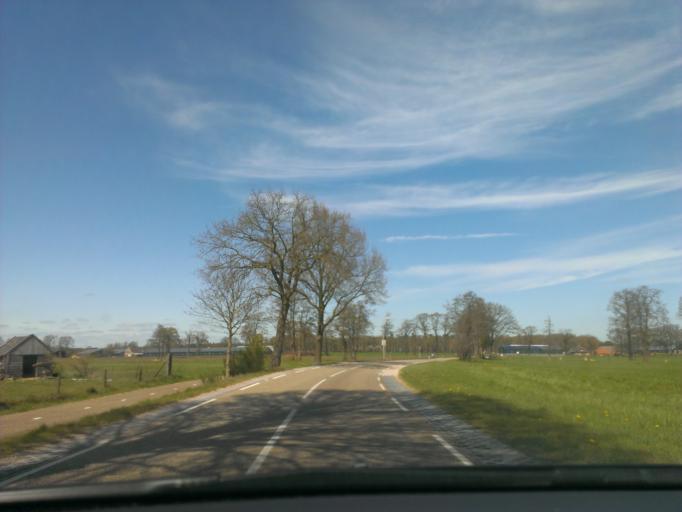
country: NL
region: Overijssel
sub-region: Gemeente Twenterand
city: Den Ham
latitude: 52.3955
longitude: 6.4547
